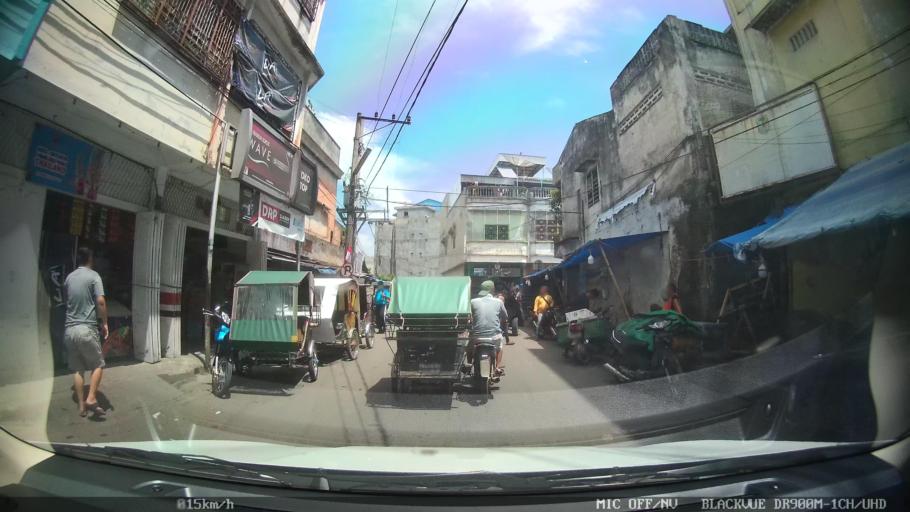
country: ID
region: North Sumatra
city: Binjai
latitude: 3.6062
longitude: 98.4877
